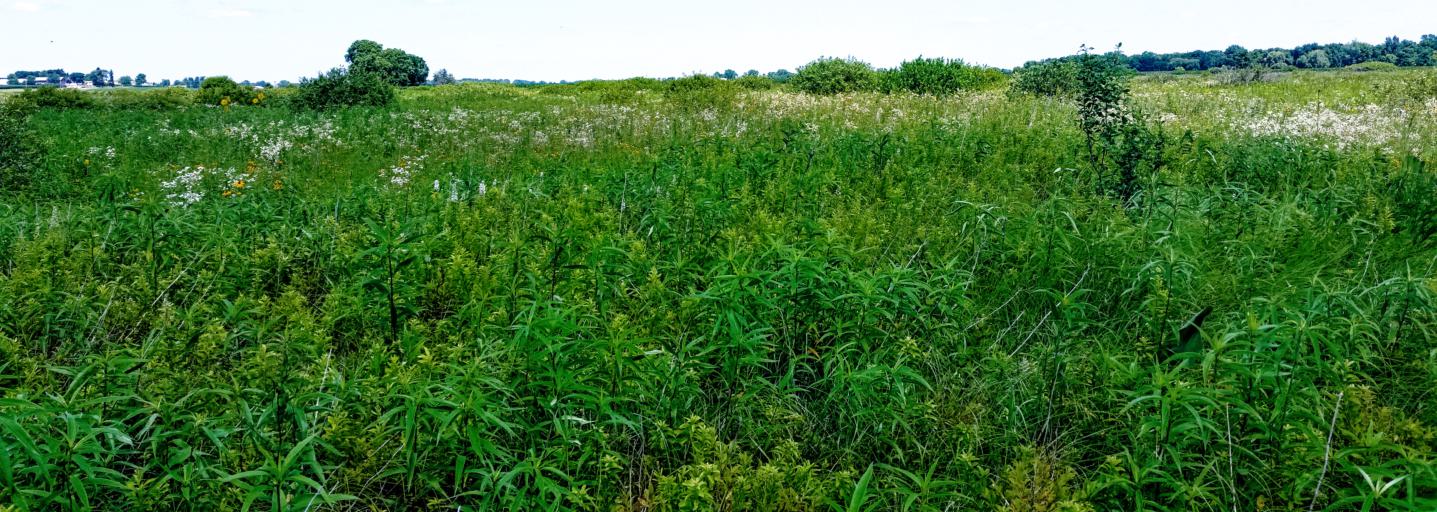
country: US
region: Wisconsin
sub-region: Jefferson County
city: Lake Mills
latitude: 43.1615
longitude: -88.8900
